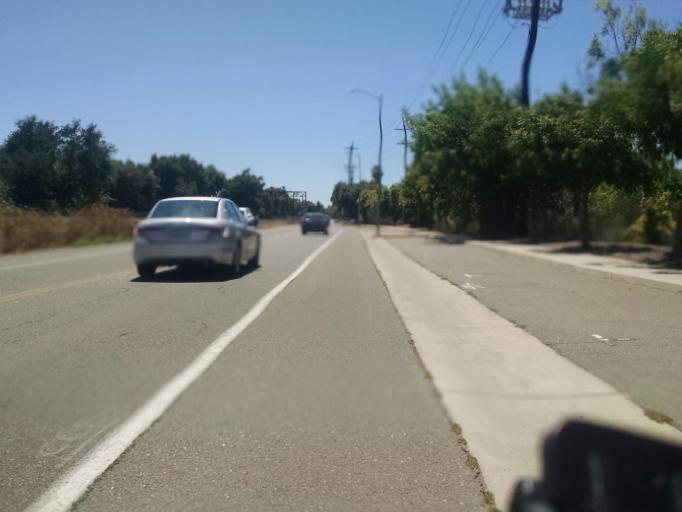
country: US
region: California
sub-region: Yolo County
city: Davis
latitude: 38.5460
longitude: -121.7291
